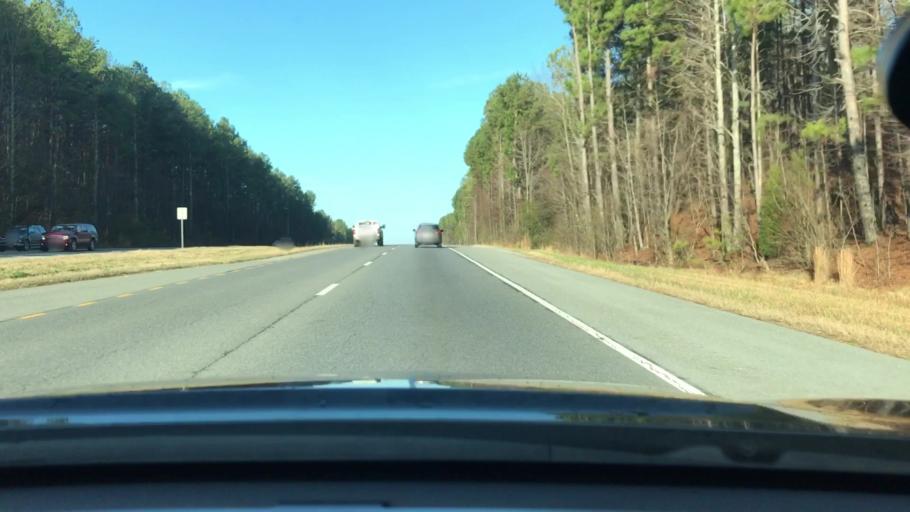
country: US
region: Alabama
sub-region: Shelby County
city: Harpersville
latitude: 33.3540
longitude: -86.4818
